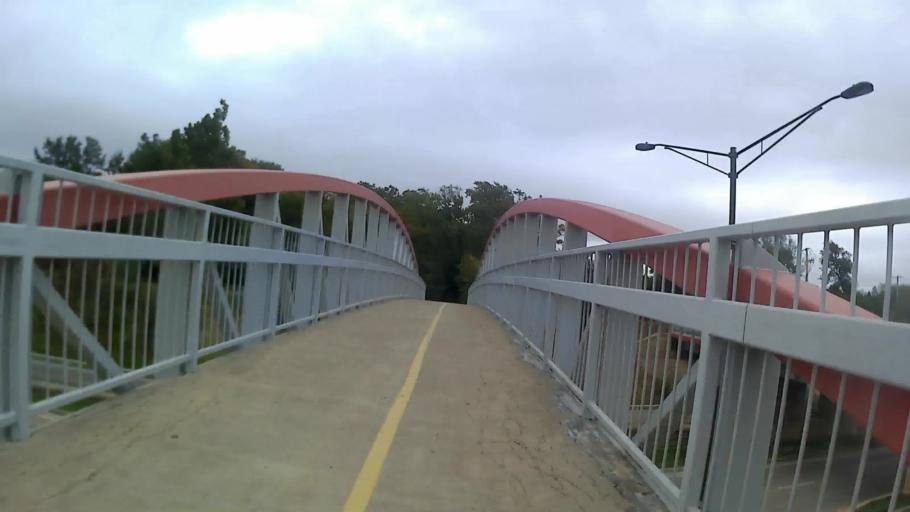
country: US
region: Illinois
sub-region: Kane County
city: Montgomery
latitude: 41.7509
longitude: -88.3759
